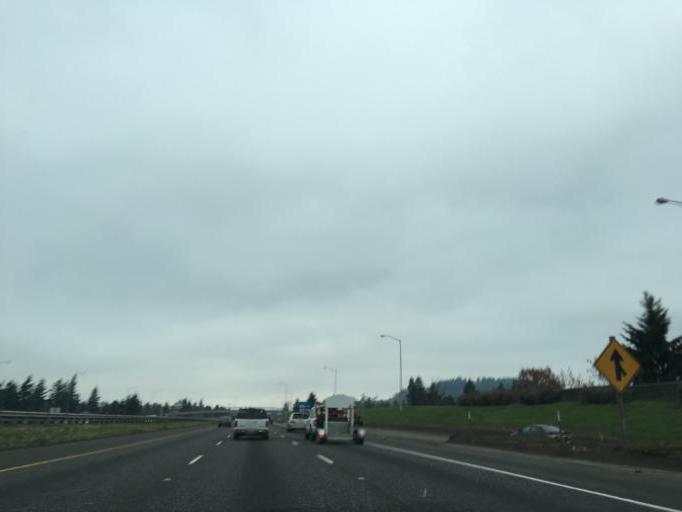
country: US
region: Oregon
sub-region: Multnomah County
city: Lents
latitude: 45.4805
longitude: -122.5657
